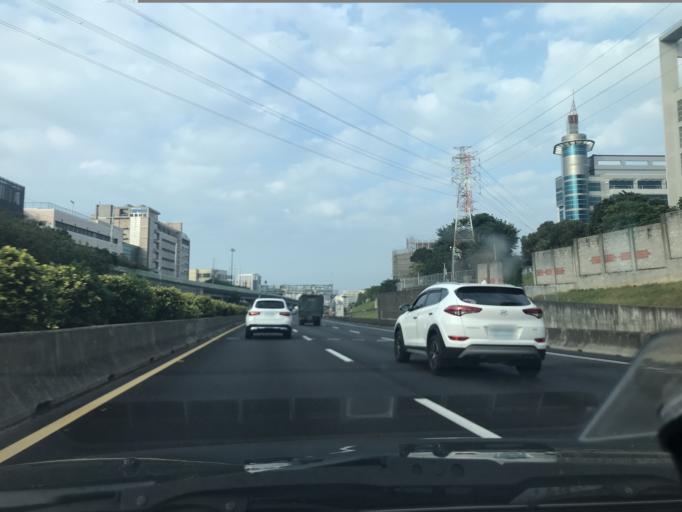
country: TW
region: Taiwan
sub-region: Hsinchu
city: Hsinchu
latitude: 24.7823
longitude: 121.0035
